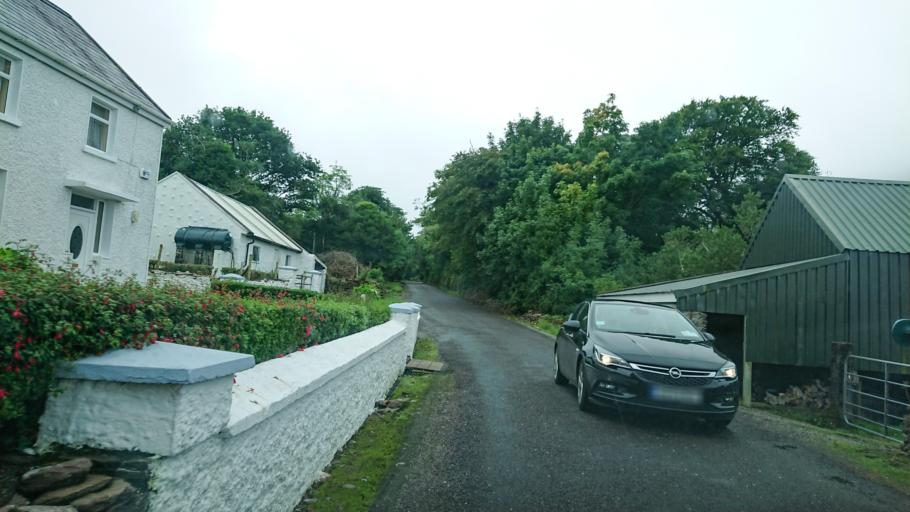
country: IE
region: Munster
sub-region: Ciarrai
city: Cahersiveen
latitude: 52.0198
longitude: -10.0975
